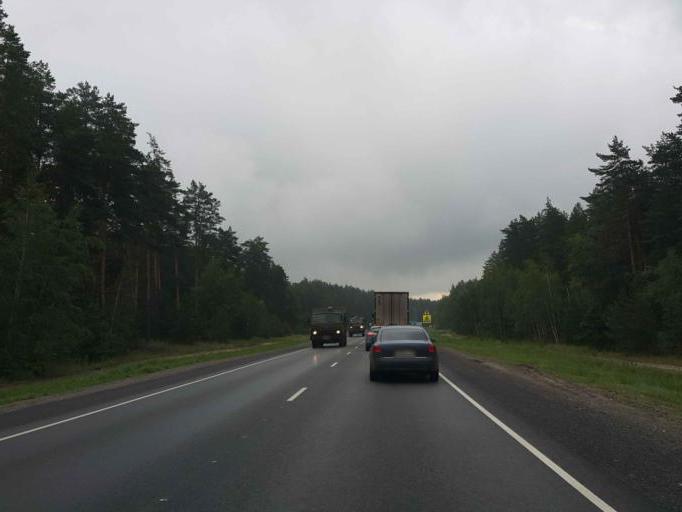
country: RU
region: Tambov
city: Novaya Lyada
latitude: 52.6938
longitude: 41.7544
